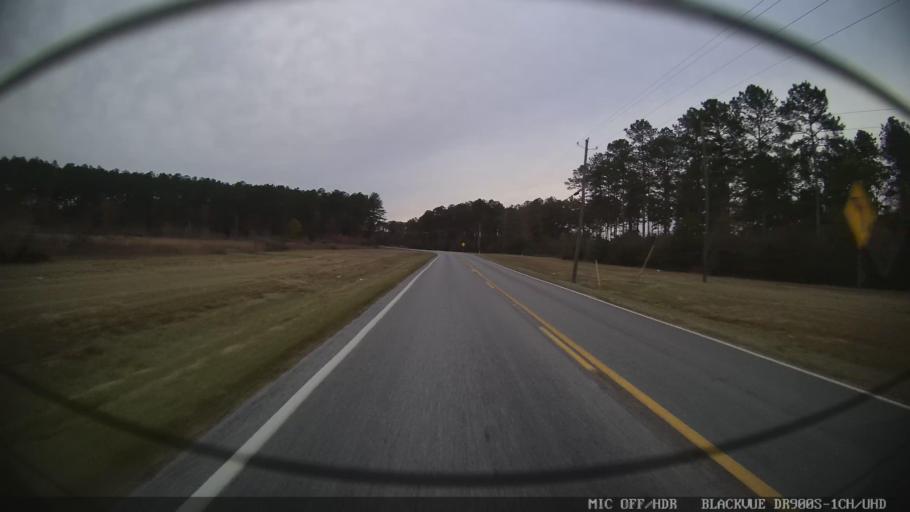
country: US
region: Mississippi
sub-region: Clarke County
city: Quitman
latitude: 32.0428
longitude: -88.7478
